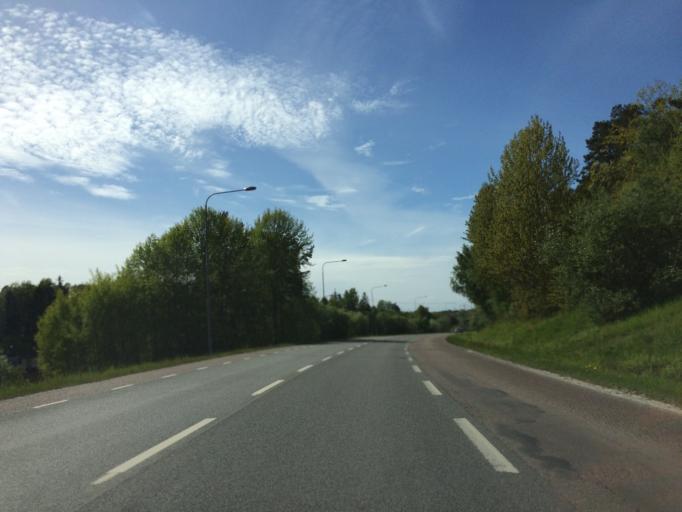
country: SE
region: Stockholm
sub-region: Sollentuna Kommun
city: Sollentuna
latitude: 59.4416
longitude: 17.9732
